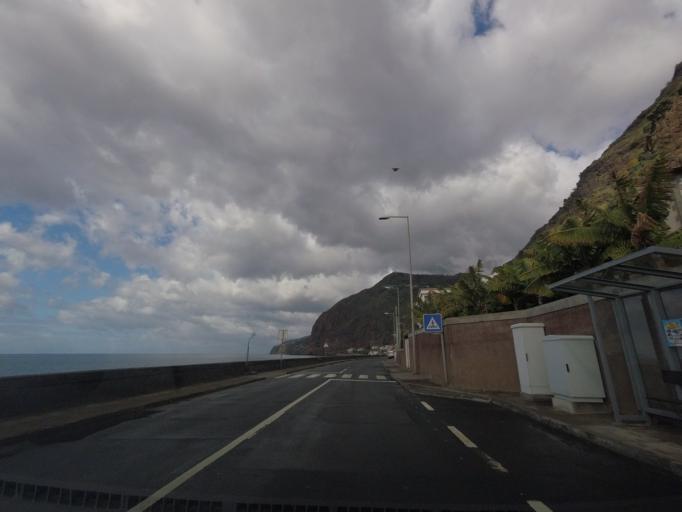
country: PT
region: Madeira
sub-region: Calheta
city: Arco da Calheta
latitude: 32.6944
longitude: -17.1268
